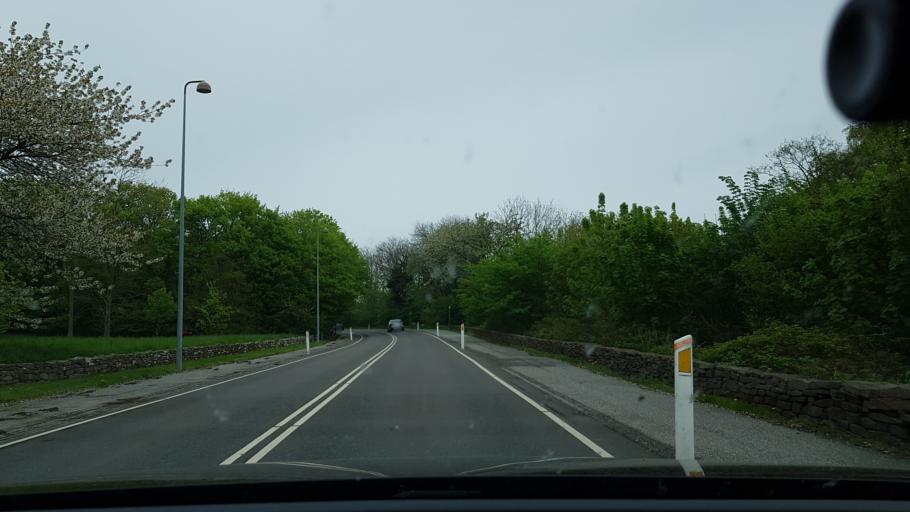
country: DK
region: Capital Region
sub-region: Bornholm Kommune
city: Nexo
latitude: 55.0752
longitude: 15.1439
